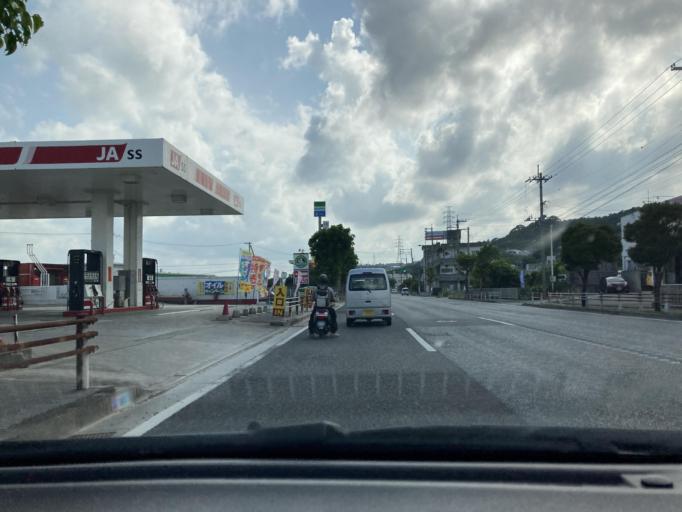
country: JP
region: Okinawa
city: Ginowan
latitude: 26.2627
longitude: 127.7887
